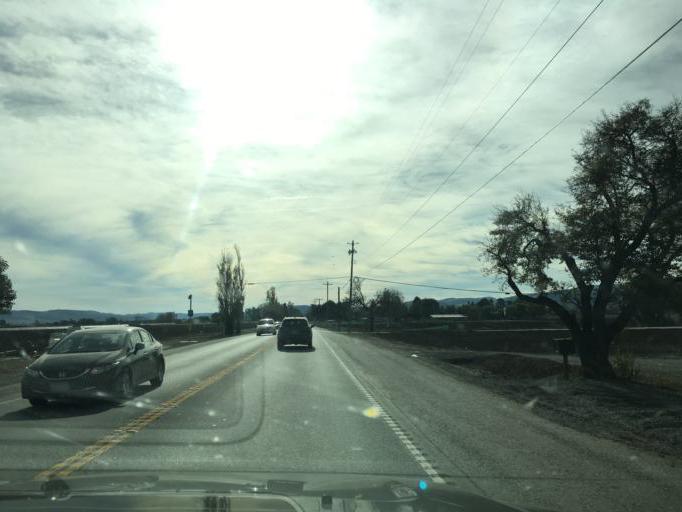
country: US
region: California
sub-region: Santa Clara County
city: Gilroy
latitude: 37.0064
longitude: -121.5189
